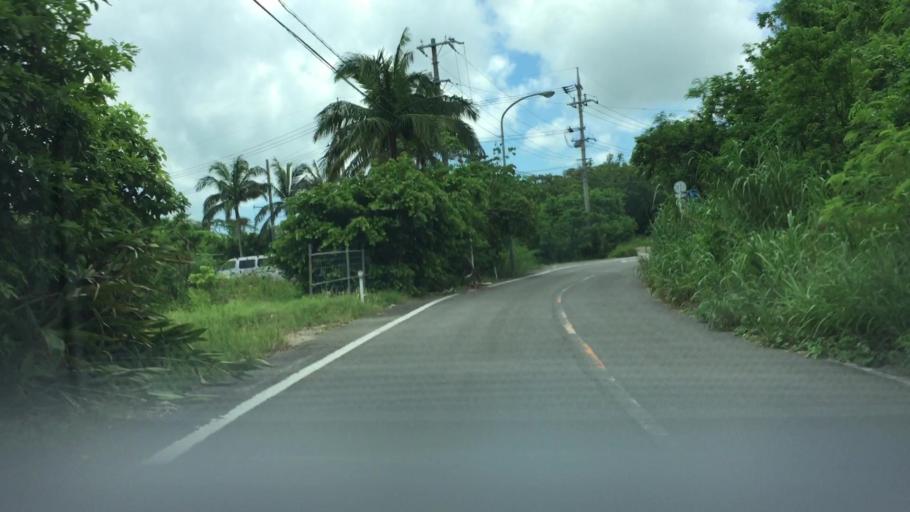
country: JP
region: Okinawa
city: Ishigaki
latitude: 24.3778
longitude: 124.1312
